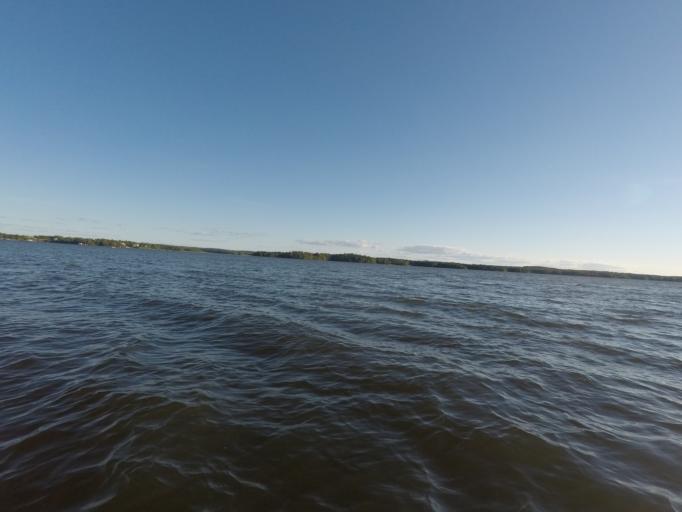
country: SE
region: Soedermanland
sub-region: Eskilstuna Kommun
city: Hallbybrunn
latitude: 59.4656
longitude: 16.4066
